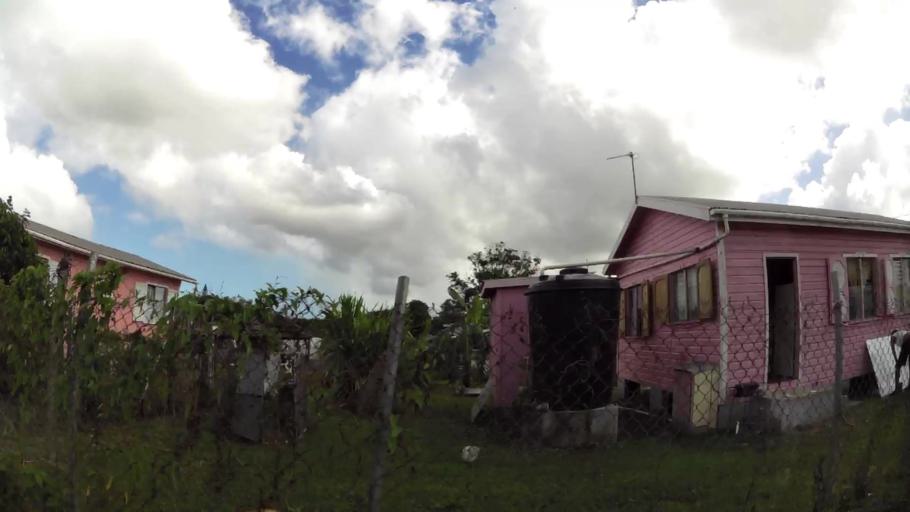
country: AG
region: Saint John
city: Saint John's
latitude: 17.1129
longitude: -61.8564
